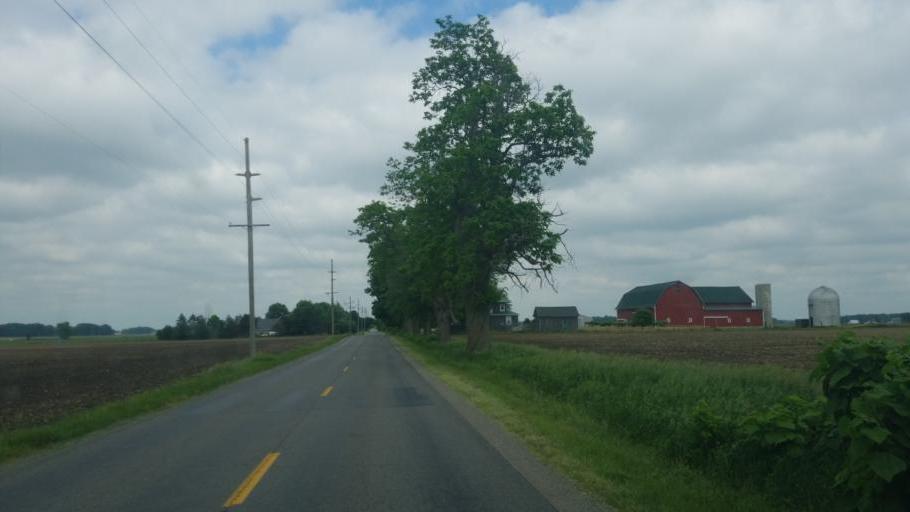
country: US
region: Indiana
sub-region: Elkhart County
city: Wakarusa
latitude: 41.4935
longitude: -86.0152
